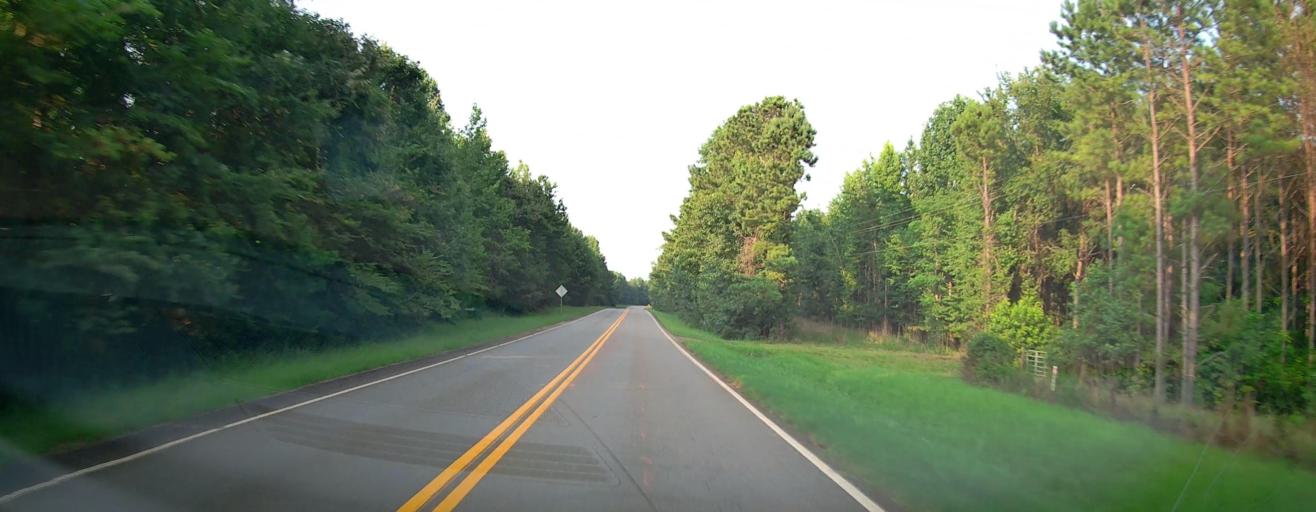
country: US
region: Georgia
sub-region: Jones County
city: Gray
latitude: 33.0608
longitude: -83.5878
